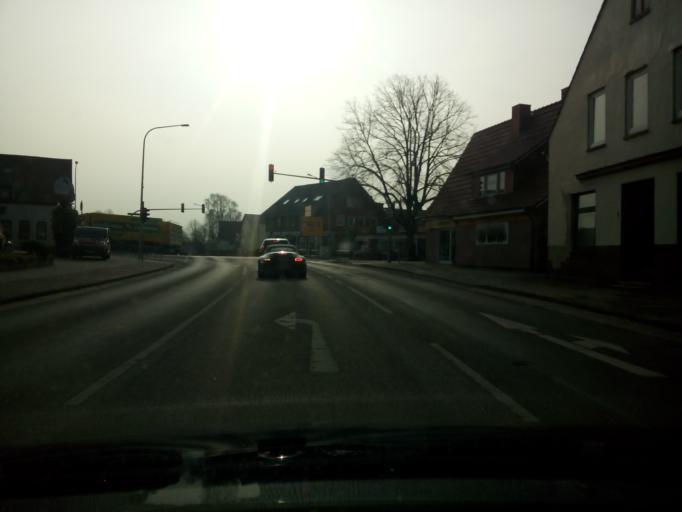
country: DE
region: Lower Saxony
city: Langen
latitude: 53.6086
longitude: 8.5945
